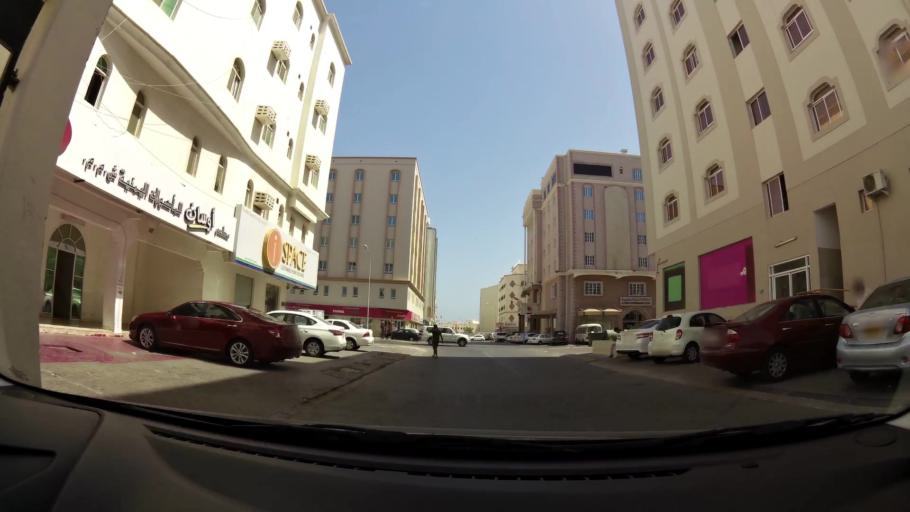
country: OM
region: Muhafazat Masqat
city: Bawshar
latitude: 23.5914
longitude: 58.4022
